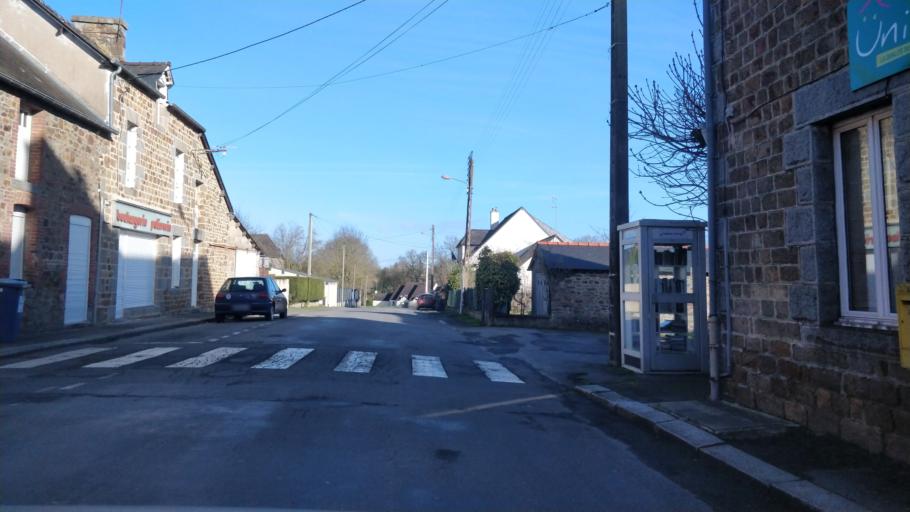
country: FR
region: Brittany
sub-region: Departement d'Ille-et-Vilaine
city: Sens-de-Bretagne
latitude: 48.3427
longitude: -1.4882
